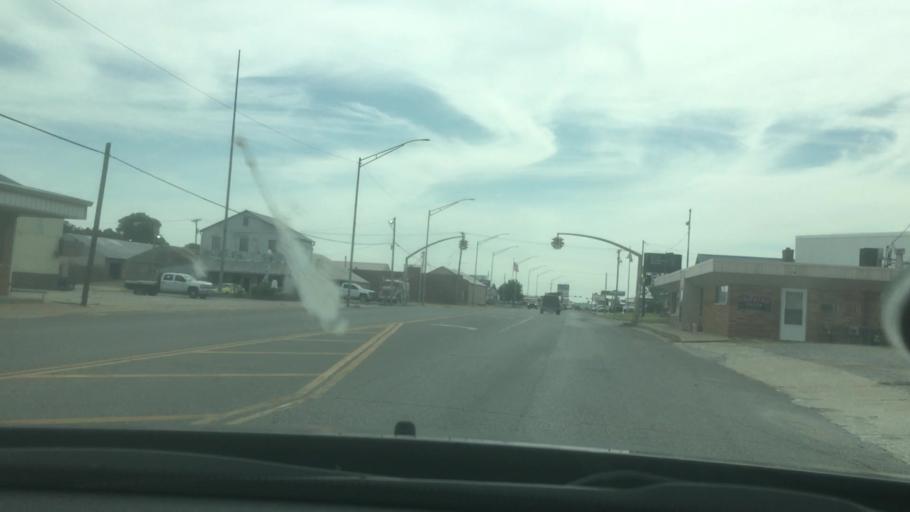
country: US
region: Oklahoma
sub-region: Garvin County
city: Lindsay
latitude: 34.8368
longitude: -97.6036
